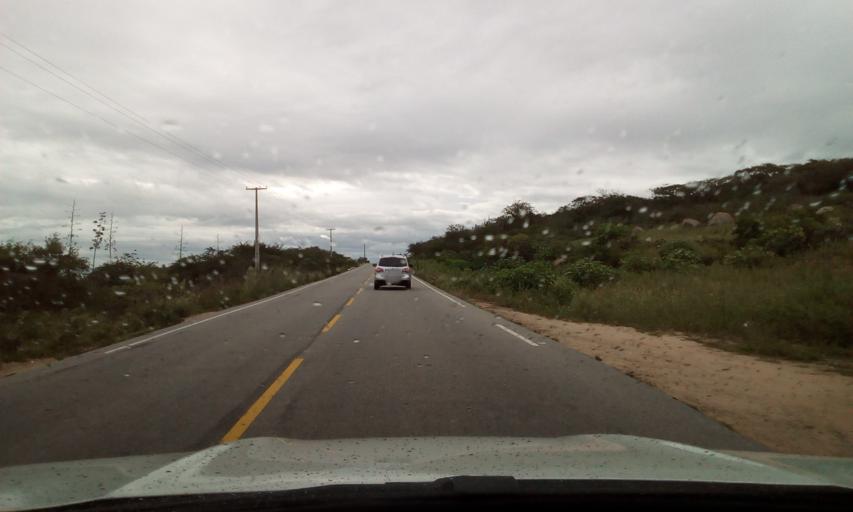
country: BR
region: Paraiba
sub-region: Picui
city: Picui
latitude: -6.5734
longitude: -36.2674
